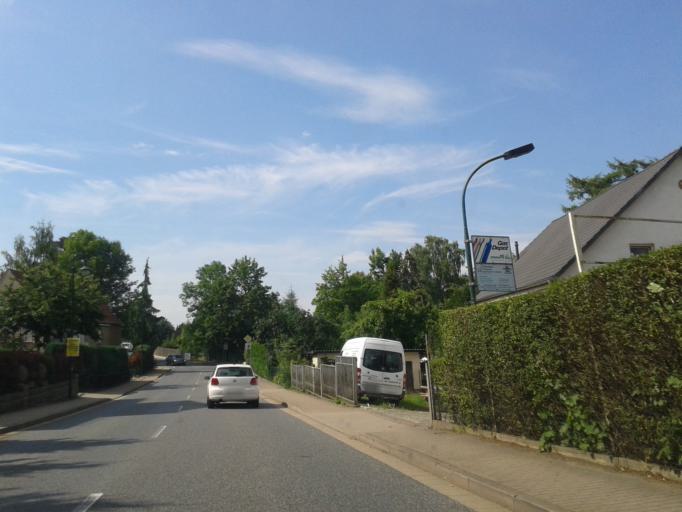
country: DE
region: Saxony
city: Wilsdruff
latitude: 51.0543
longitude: 13.5345
